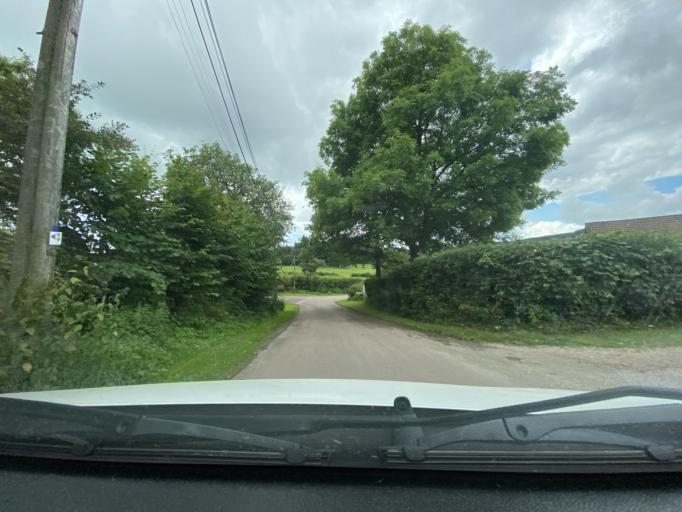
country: FR
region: Bourgogne
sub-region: Departement de la Cote-d'Or
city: Saulieu
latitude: 47.2616
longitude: 4.1875
